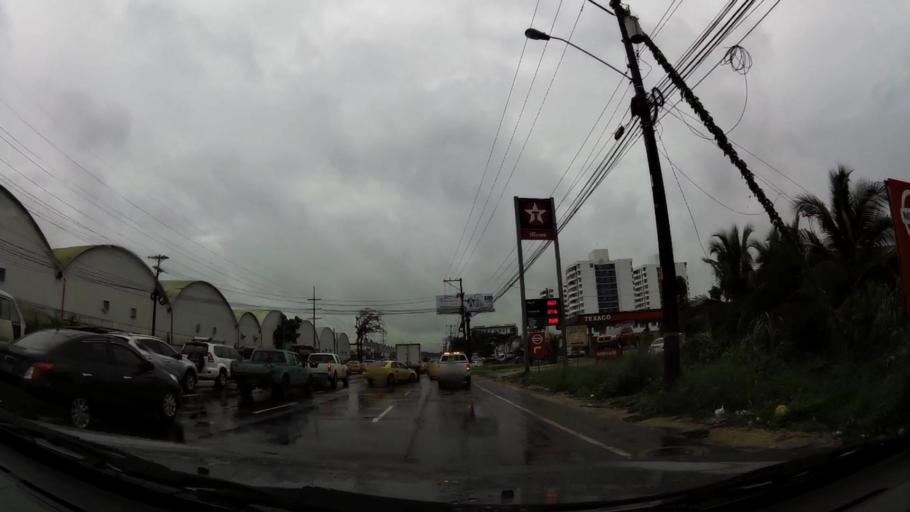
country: PA
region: Colon
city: Arco Iris
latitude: 9.3402
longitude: -79.8768
